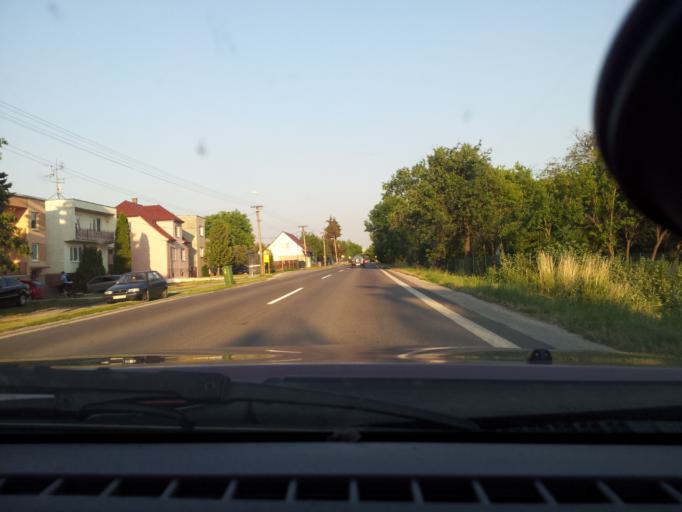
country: SK
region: Trnavsky
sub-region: Okres Skalica
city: Skalica
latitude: 48.7720
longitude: 17.2733
